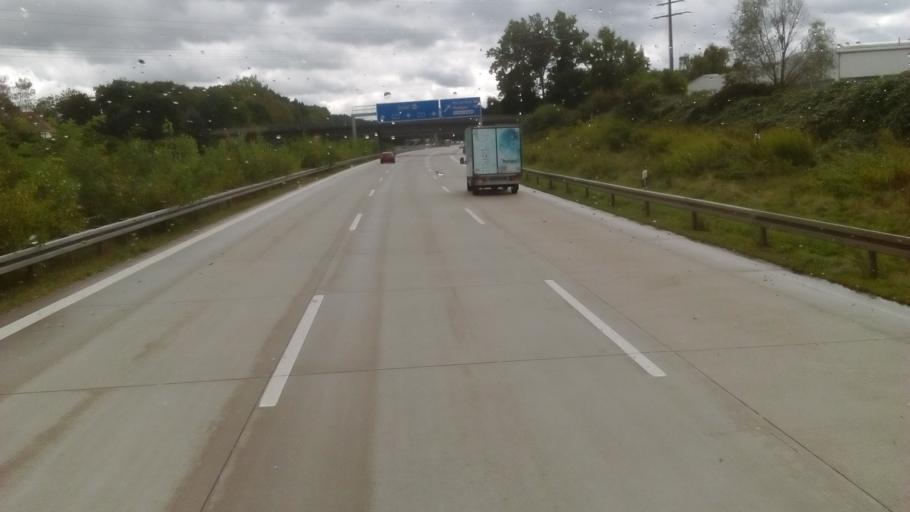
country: FR
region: Alsace
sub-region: Departement du Haut-Rhin
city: Huningue
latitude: 47.6063
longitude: 7.5989
